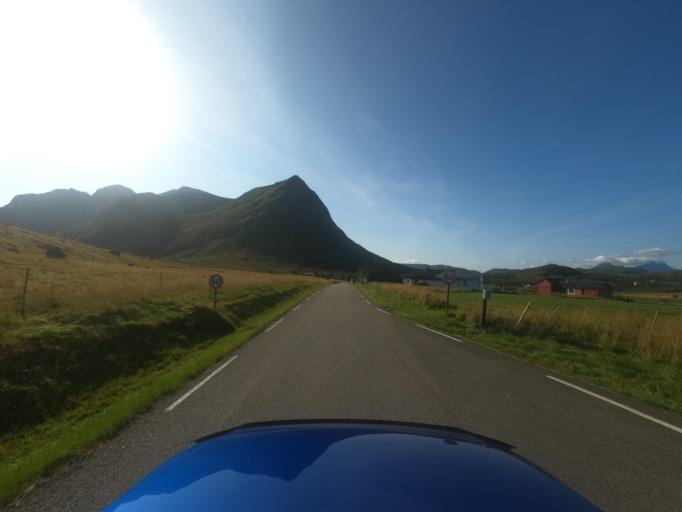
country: NO
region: Nordland
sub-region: Vestvagoy
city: Evjen
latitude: 68.3253
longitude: 13.9192
